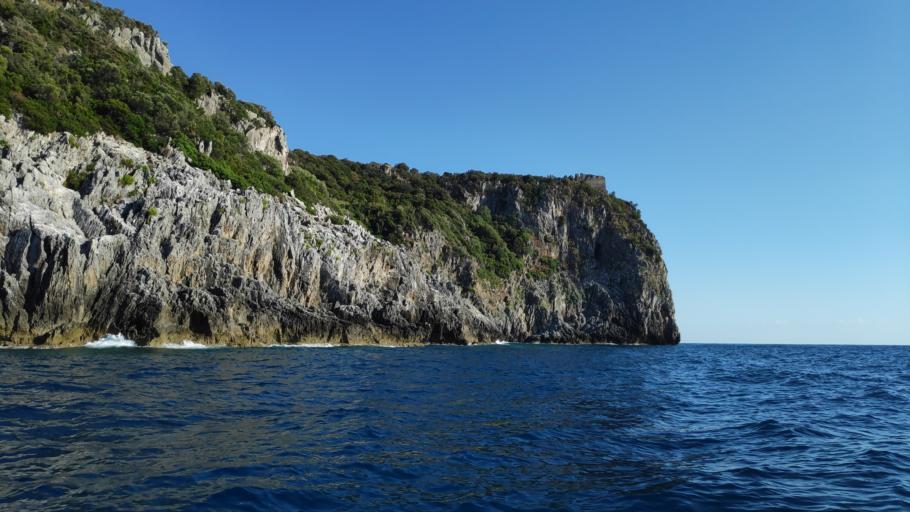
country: IT
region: Calabria
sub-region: Provincia di Cosenza
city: Praia a Mare
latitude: 39.8749
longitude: 15.7700
